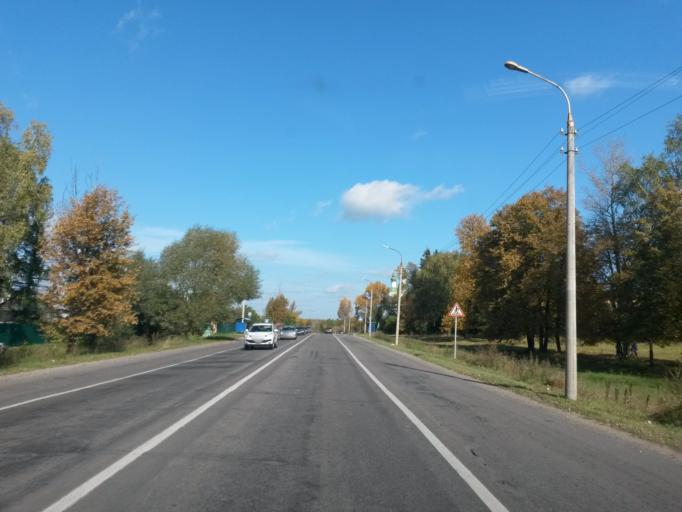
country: RU
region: Moskovskaya
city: Stolbovaya
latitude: 55.2725
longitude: 37.5107
